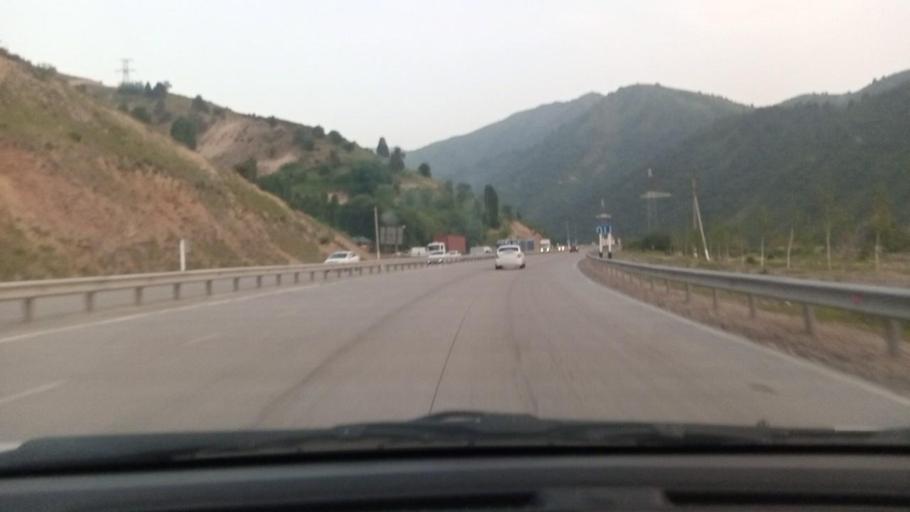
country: UZ
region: Toshkent
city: Angren
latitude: 41.1499
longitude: 70.4461
